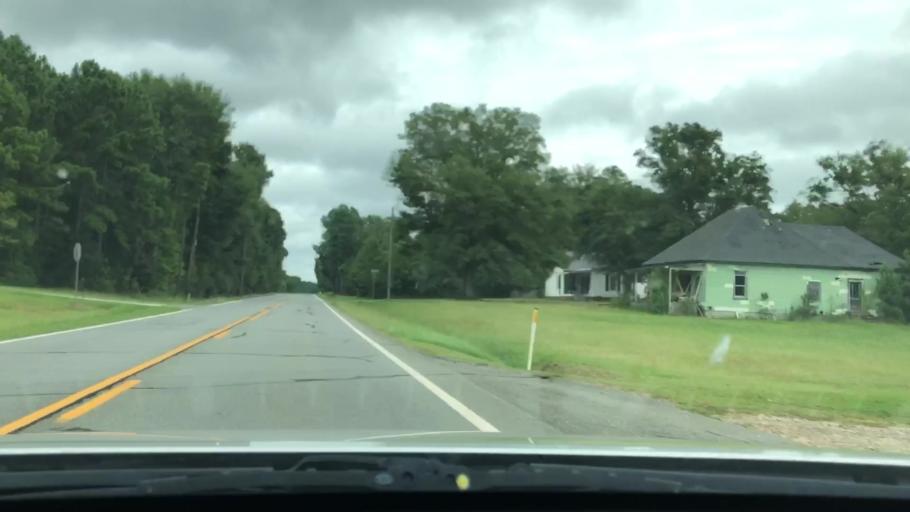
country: US
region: Georgia
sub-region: Pike County
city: Zebulon
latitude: 33.0506
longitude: -84.4862
